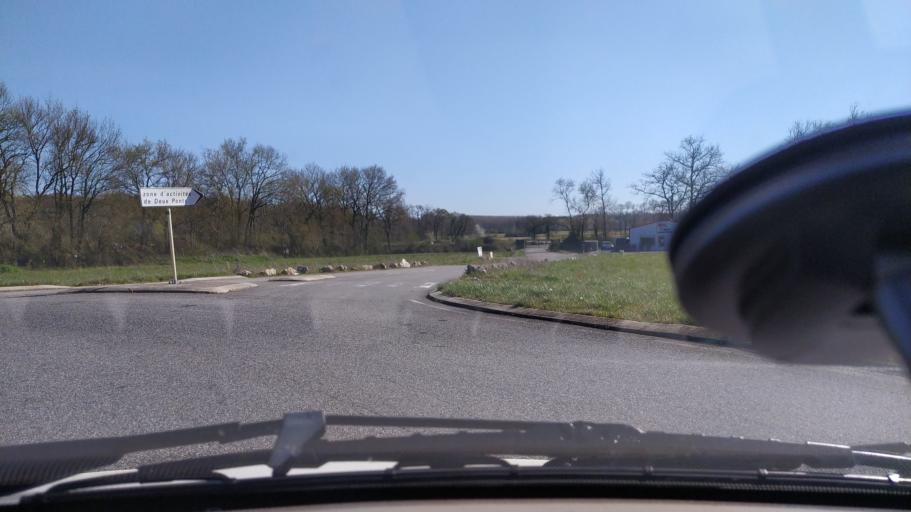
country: FR
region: Midi-Pyrenees
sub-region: Departement du Gers
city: Nogaro
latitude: 43.7507
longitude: -0.0918
